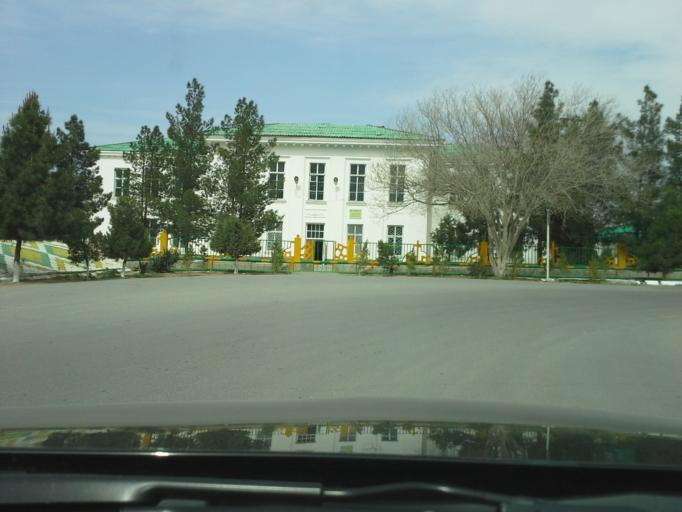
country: TM
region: Ahal
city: Abadan
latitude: 38.0623
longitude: 58.1550
